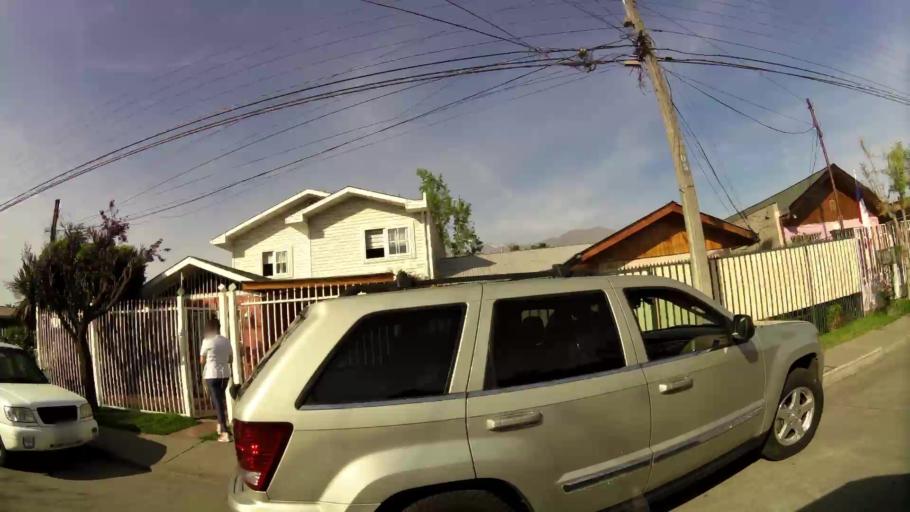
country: CL
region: Santiago Metropolitan
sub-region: Provincia de Santiago
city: La Pintana
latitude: -33.5316
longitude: -70.5862
